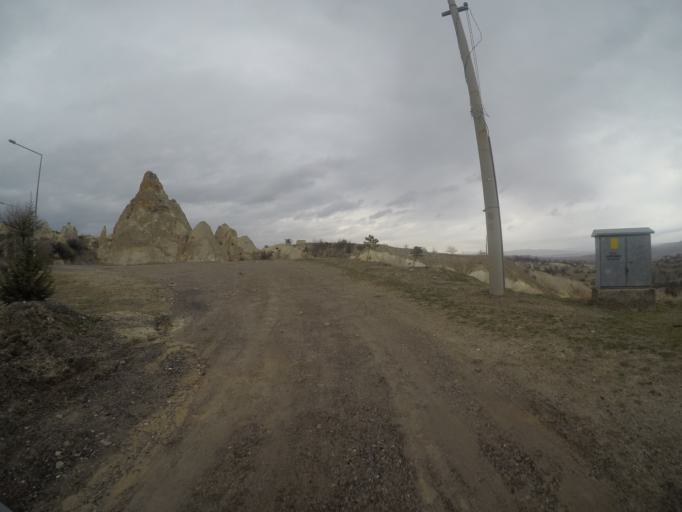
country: TR
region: Nevsehir
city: Urgub
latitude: 38.6338
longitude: 34.8942
